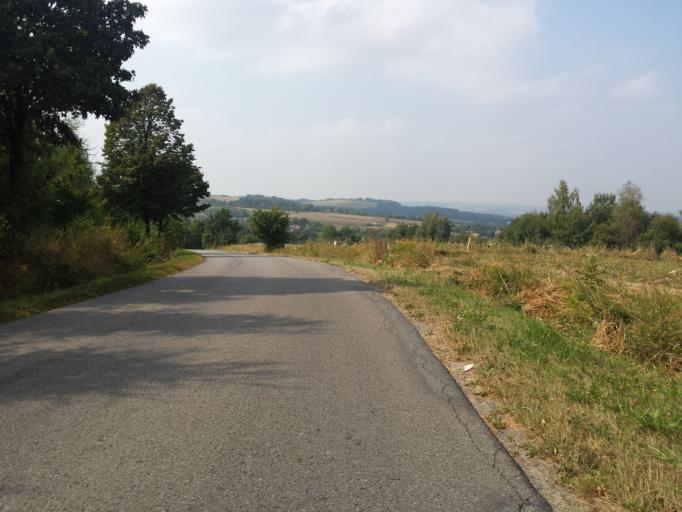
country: PL
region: Subcarpathian Voivodeship
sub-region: Powiat rzeszowski
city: Blazowa
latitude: 49.8427
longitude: 22.1480
